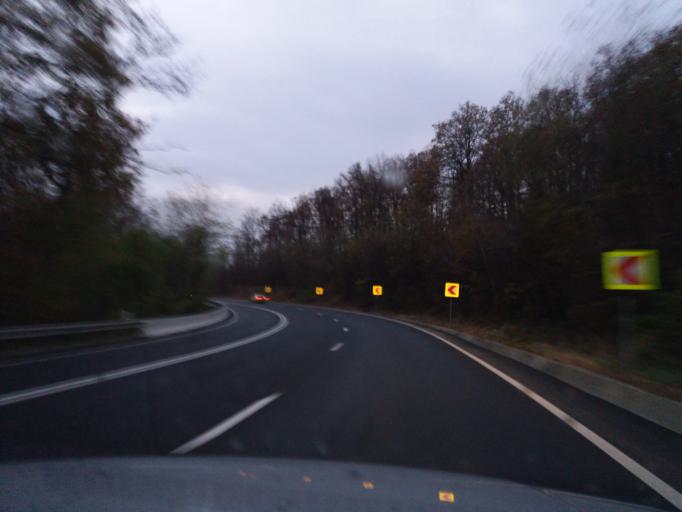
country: RO
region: Hunedoara
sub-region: Comuna Santamaria-Orlea
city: Santamaria-Orlea
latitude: 45.6168
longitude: 22.9845
